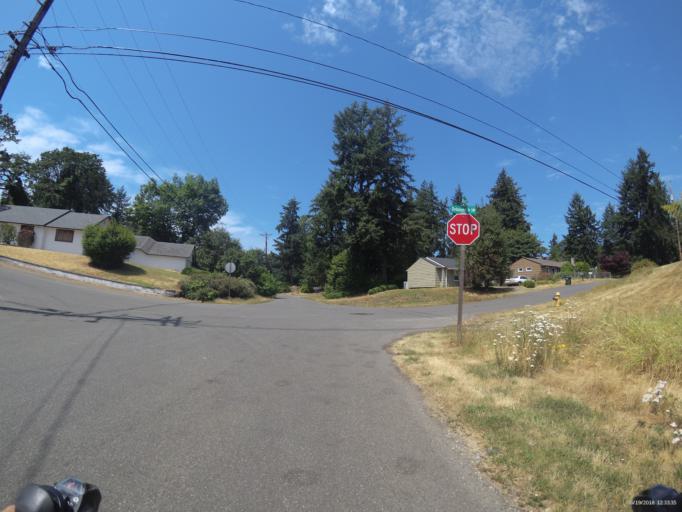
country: US
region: Washington
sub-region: Pierce County
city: Lakewood
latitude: 47.1708
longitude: -122.5289
